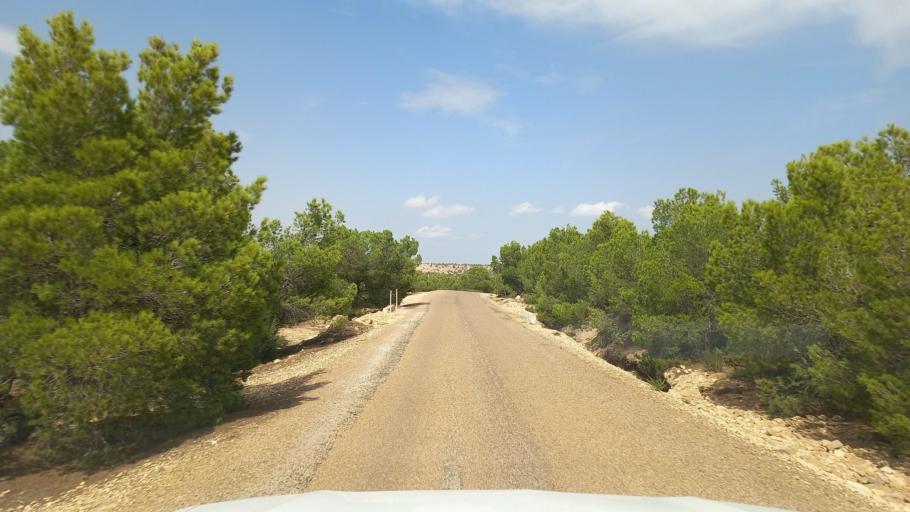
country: TN
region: Al Qasrayn
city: Sbiba
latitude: 35.4031
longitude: 8.9205
